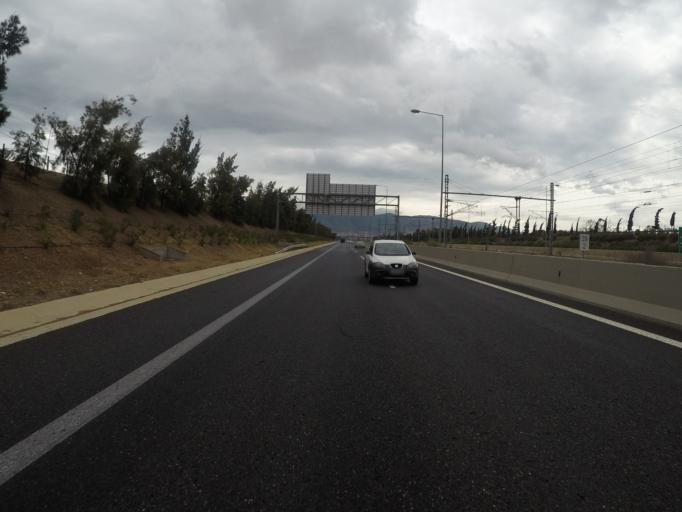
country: GR
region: Attica
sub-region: Nomarchia Dytikis Attikis
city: Magoula
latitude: 38.0794
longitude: 23.5343
